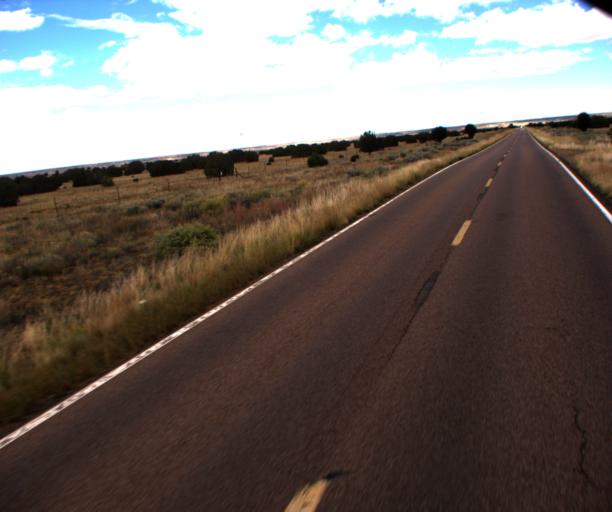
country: US
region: Arizona
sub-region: Navajo County
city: Heber-Overgaard
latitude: 34.5841
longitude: -110.4022
